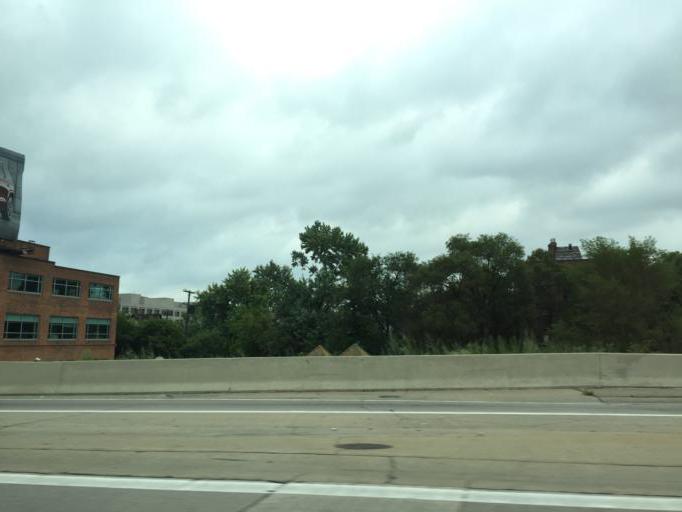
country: US
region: Michigan
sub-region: Wayne County
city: Hamtramck
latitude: 42.3608
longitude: -83.0771
